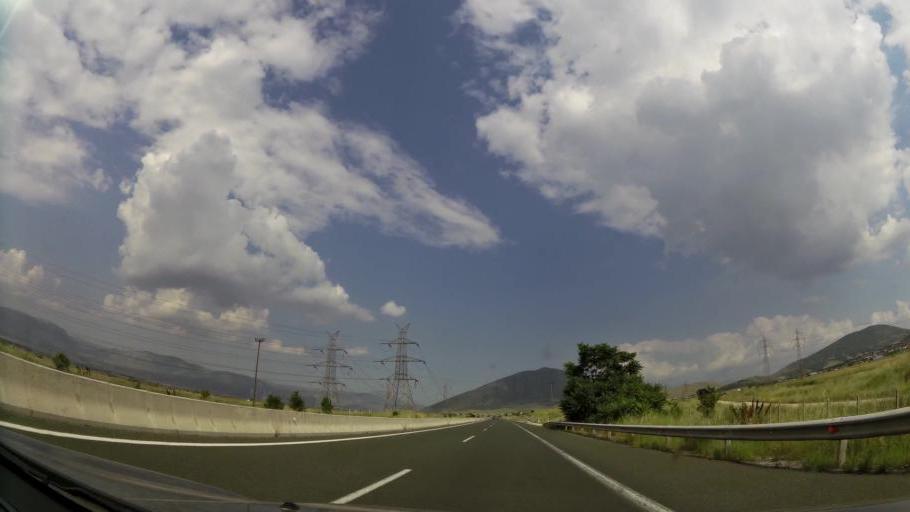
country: GR
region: West Macedonia
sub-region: Nomos Kozanis
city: Koila
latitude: 40.3620
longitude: 21.8305
